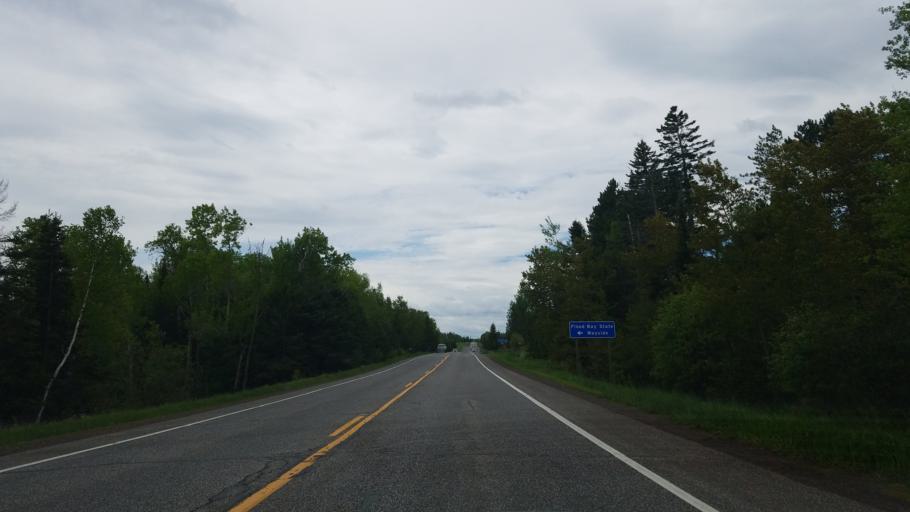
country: US
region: Minnesota
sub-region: Lake County
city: Two Harbors
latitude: 47.0406
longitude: -91.6407
